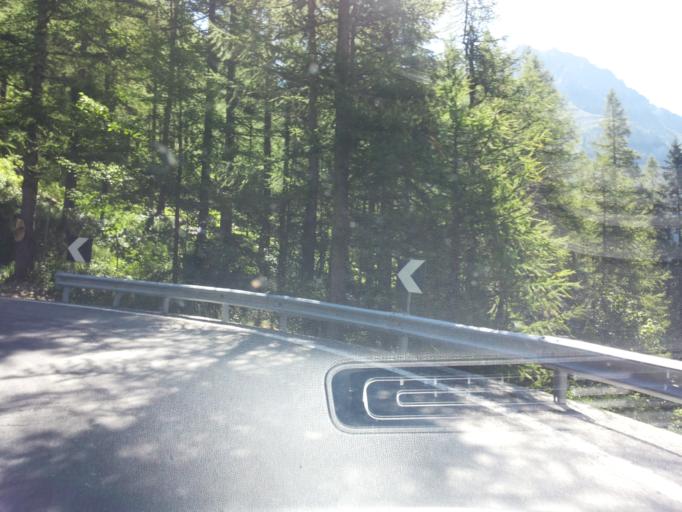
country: IT
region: Aosta Valley
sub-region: Valle d'Aosta
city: Gressoney-La-Trinite
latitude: 45.8357
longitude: 7.8197
